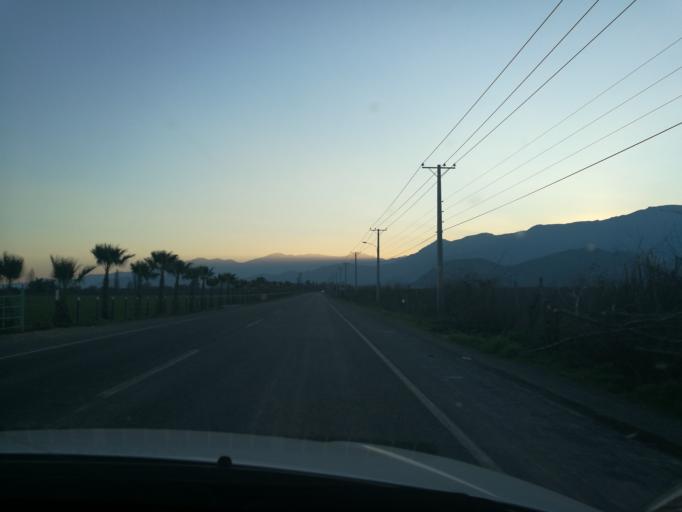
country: CL
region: O'Higgins
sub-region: Provincia de Cachapoal
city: Graneros
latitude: -34.0367
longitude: -70.6829
